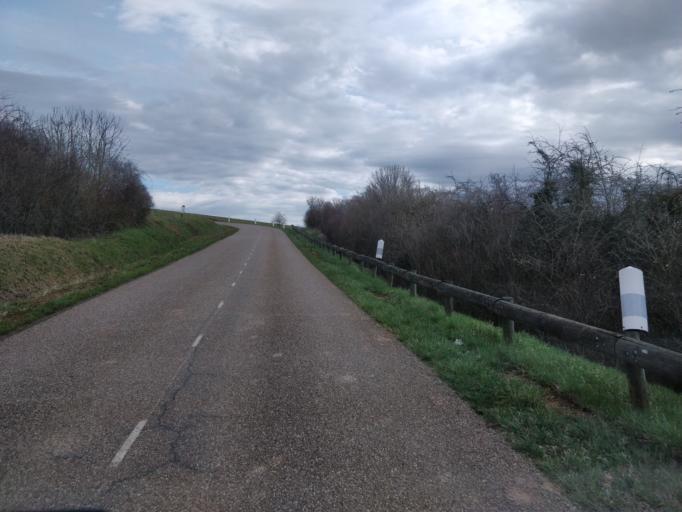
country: FR
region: Lorraine
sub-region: Departement de Meurthe-et-Moselle
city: Doncourt-les-Conflans
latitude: 49.1098
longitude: 5.9030
